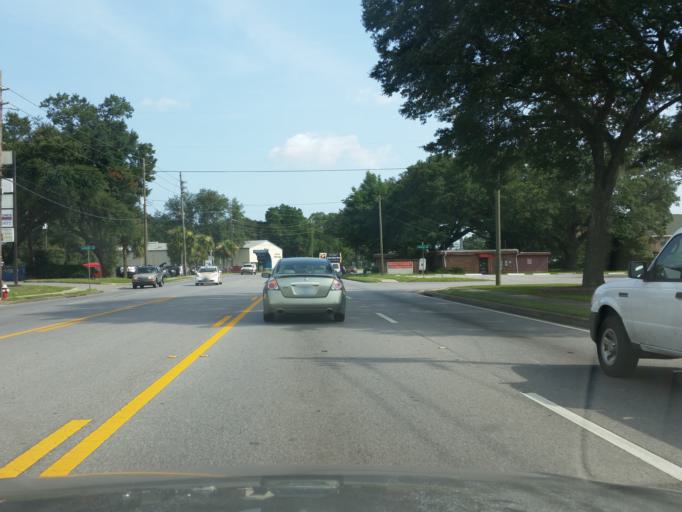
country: US
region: Florida
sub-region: Escambia County
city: Brent
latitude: 30.4673
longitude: -87.2534
